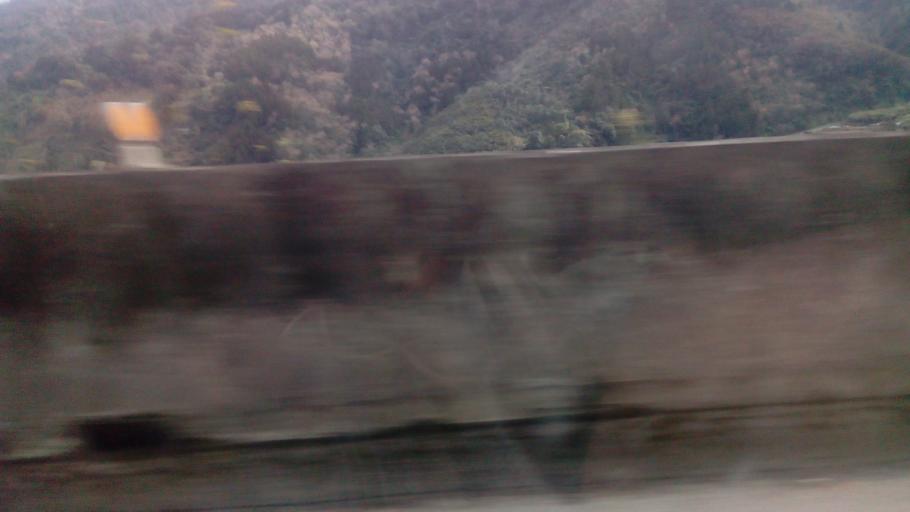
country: TW
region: Taiwan
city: Daxi
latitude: 24.4557
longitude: 121.3931
